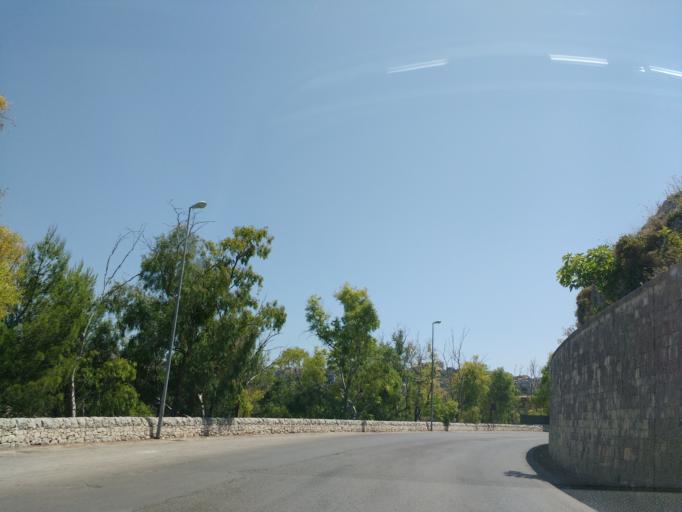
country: IT
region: Sicily
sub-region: Ragusa
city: Modica
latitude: 36.8668
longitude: 14.7515
